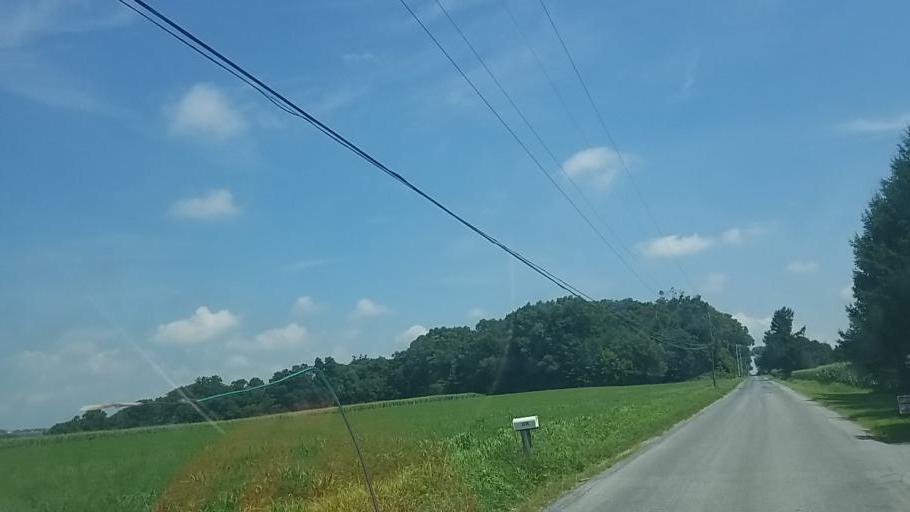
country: US
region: Pennsylvania
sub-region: Chester County
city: Atglen
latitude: 39.8826
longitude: -75.9663
